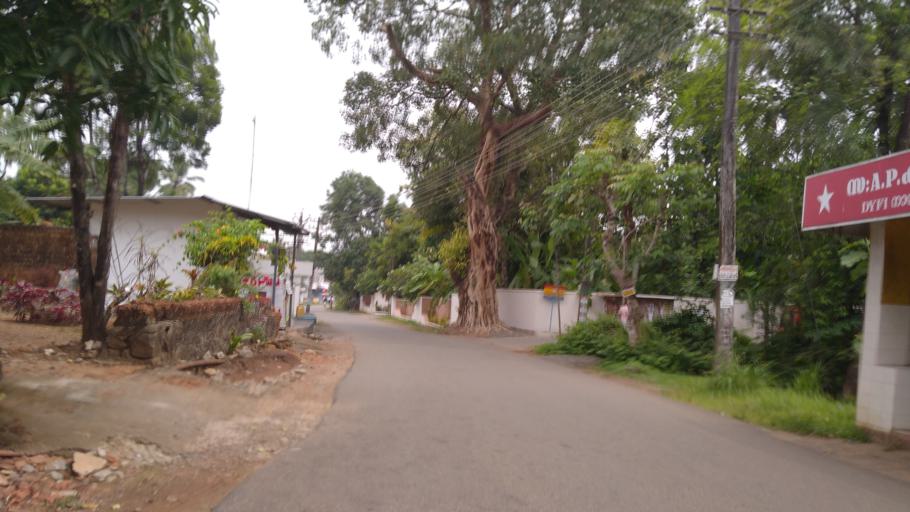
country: IN
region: Kerala
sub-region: Ernakulam
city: Angamali
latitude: 10.1644
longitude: 76.3960
